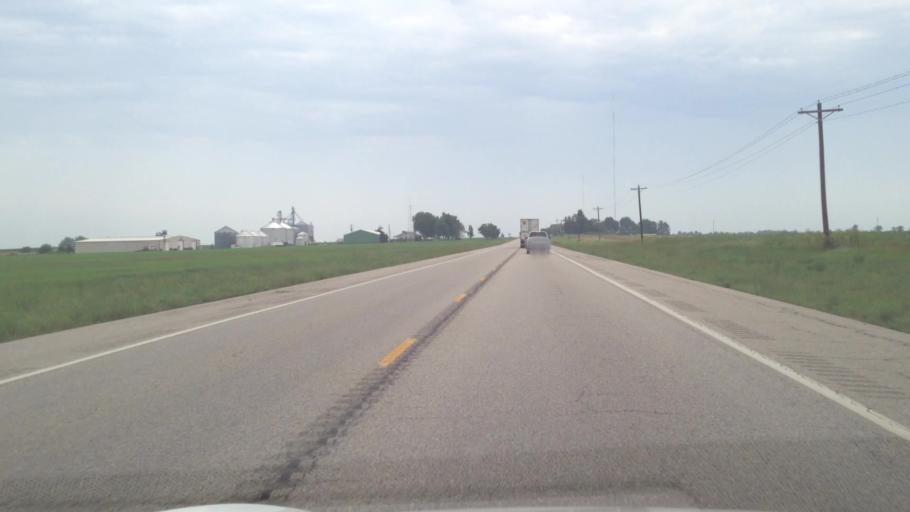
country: US
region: Missouri
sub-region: Jasper County
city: Carl Junction
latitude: 37.2419
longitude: -94.7051
